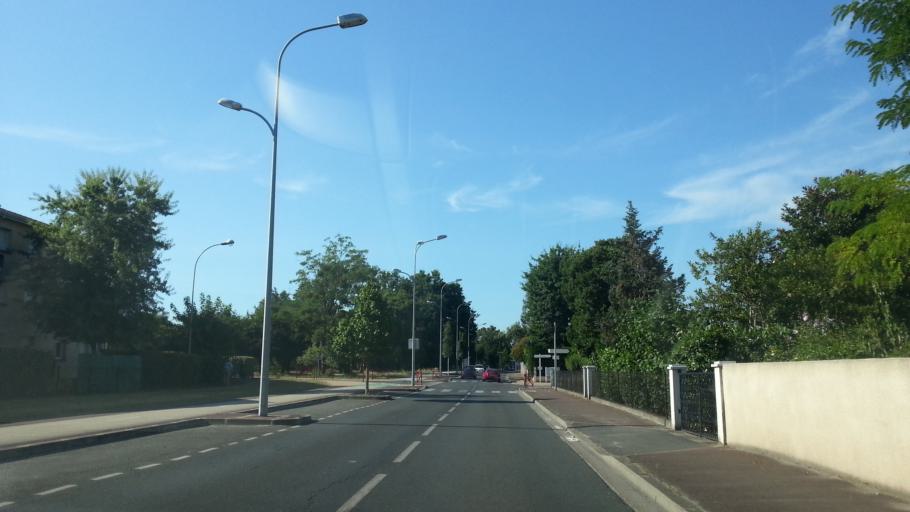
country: FR
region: Aquitaine
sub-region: Departement de la Gironde
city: Leognan
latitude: 44.7604
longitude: -0.5825
